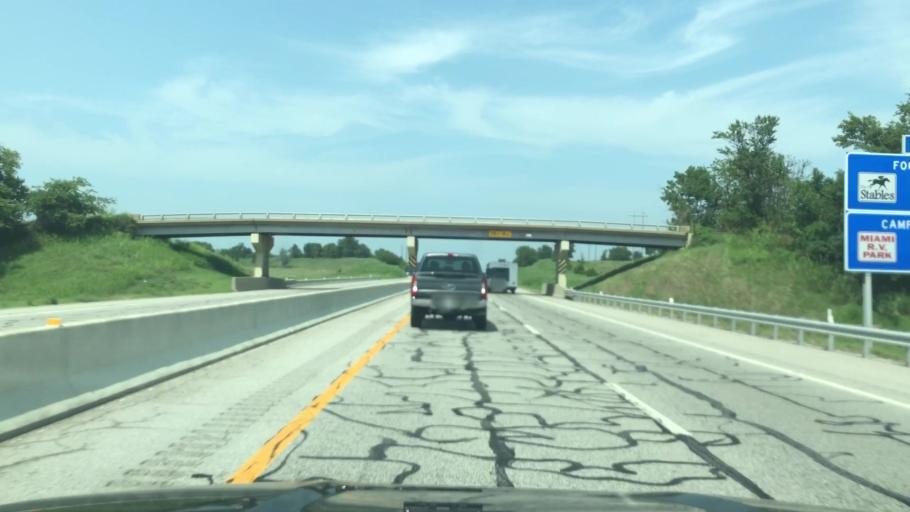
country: US
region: Oklahoma
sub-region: Ottawa County
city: Miami
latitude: 36.8295
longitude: -94.8669
